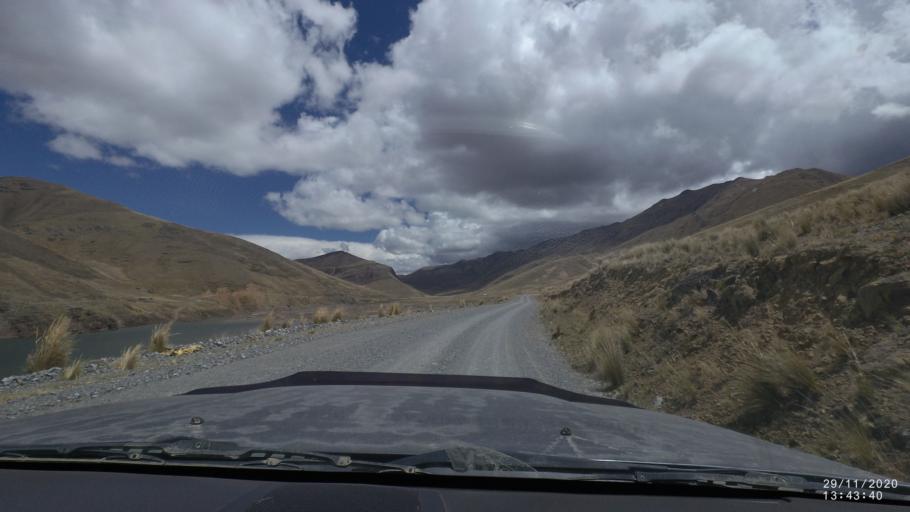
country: BO
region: Cochabamba
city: Cochabamba
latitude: -17.1408
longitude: -66.3191
